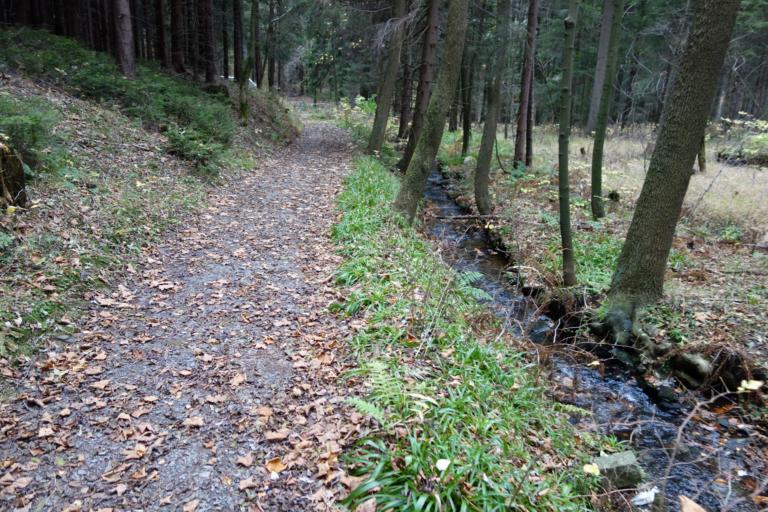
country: DE
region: Saxony
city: Kurort Oberwiesenthal
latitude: 50.4657
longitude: 12.9840
